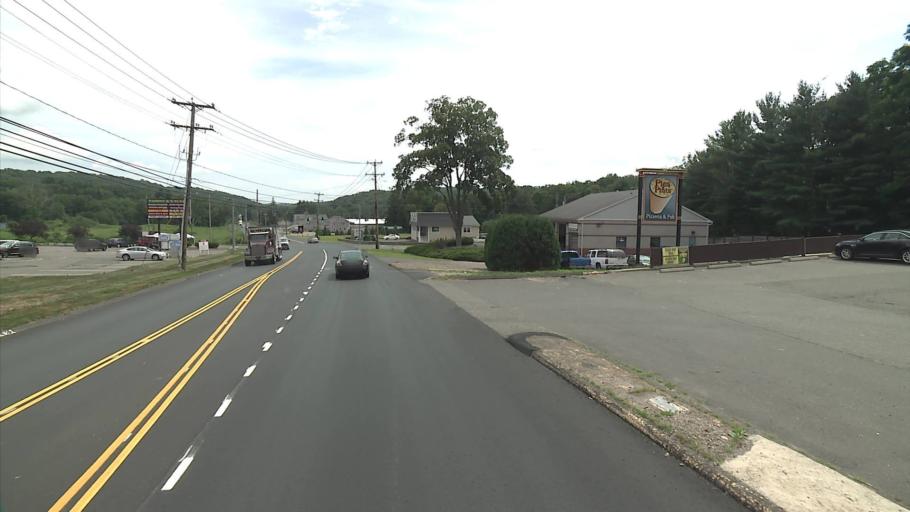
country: US
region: Connecticut
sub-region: New Haven County
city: Seymour
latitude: 41.4108
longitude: -73.0977
